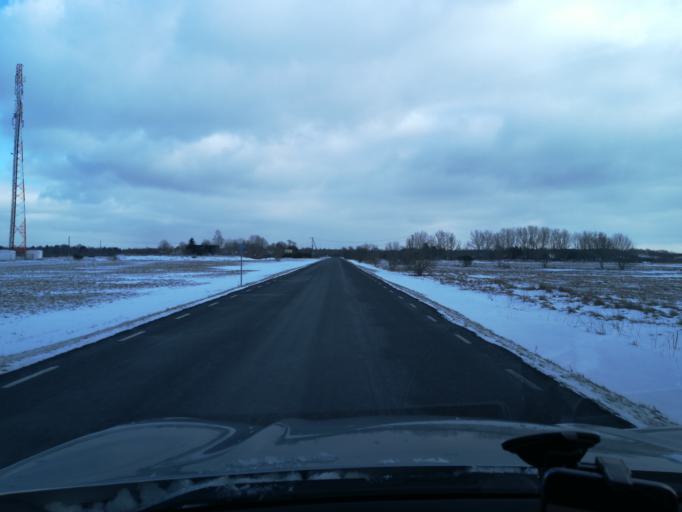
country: EE
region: Harju
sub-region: Harku vald
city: Tabasalu
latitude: 59.4292
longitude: 24.4103
